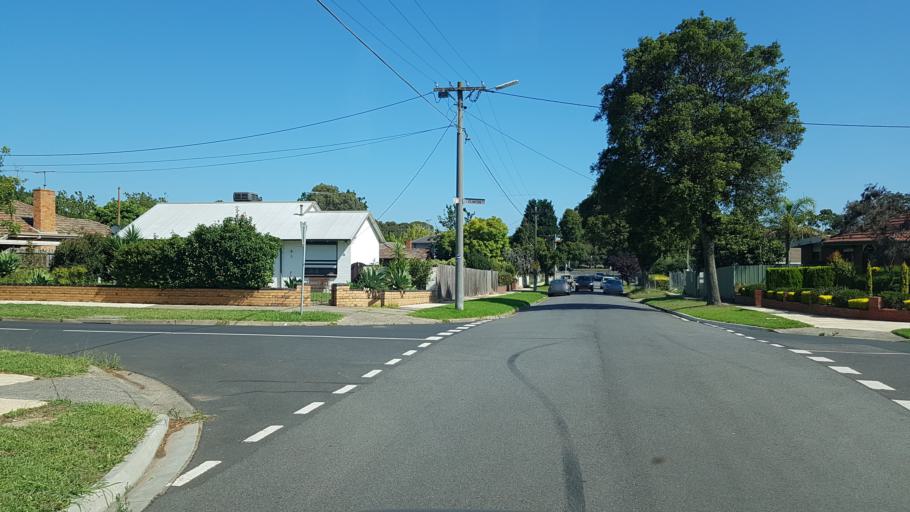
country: AU
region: Victoria
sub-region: Banyule
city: Heidelberg Heights
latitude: -37.7506
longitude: 145.0496
